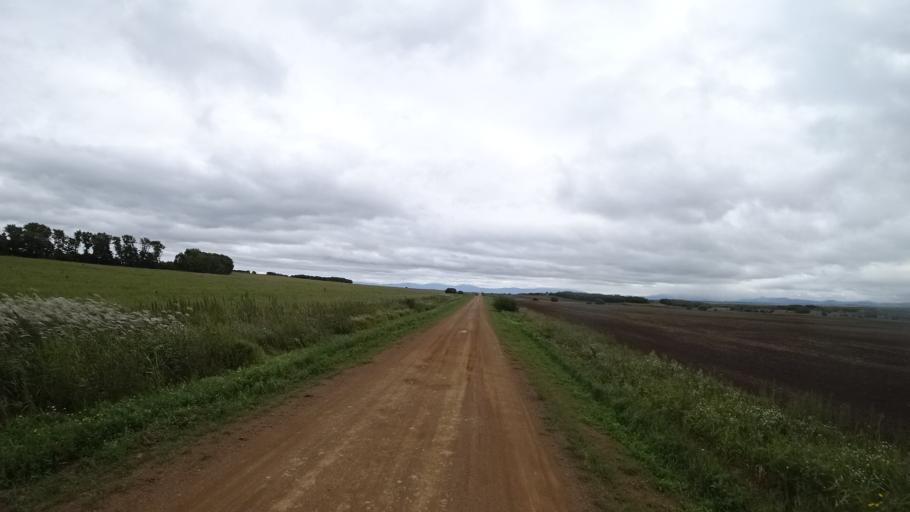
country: RU
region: Primorskiy
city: Chernigovka
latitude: 44.4373
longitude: 132.5804
